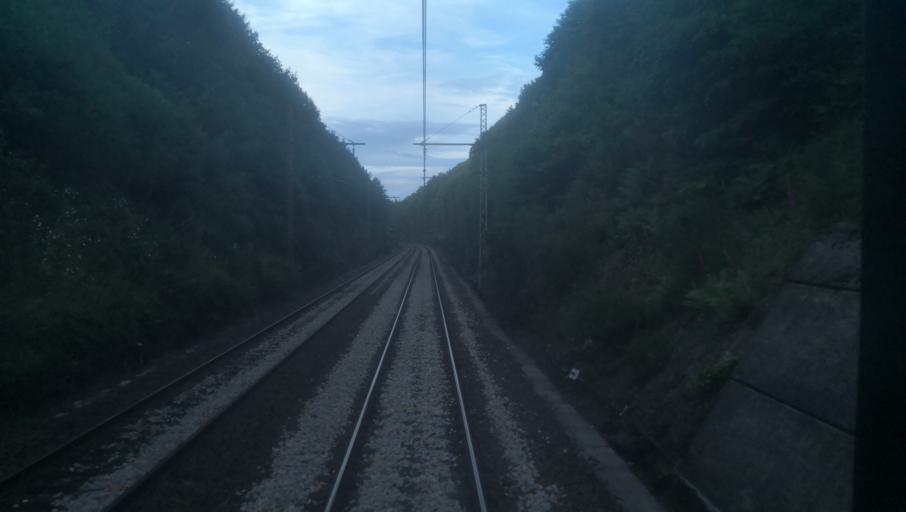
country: FR
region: Limousin
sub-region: Departement de la Creuse
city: Saint-Agnant-de-Versillat
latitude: 46.3117
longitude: 1.5155
